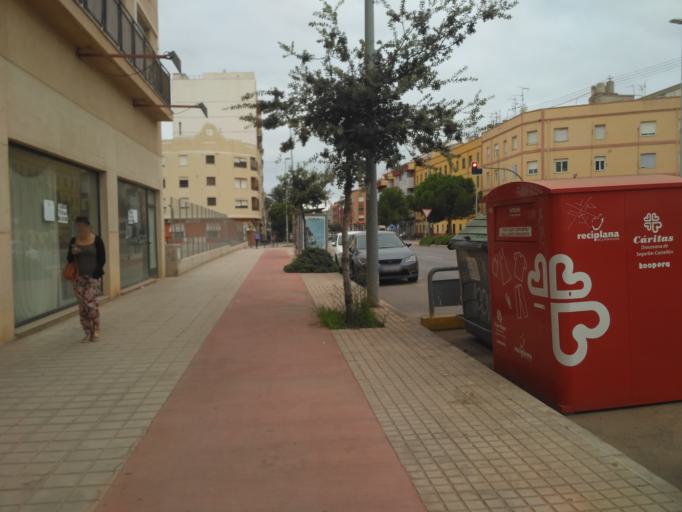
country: ES
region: Valencia
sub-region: Provincia de Castello
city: Castello de la Plana
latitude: 39.9879
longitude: -0.0636
